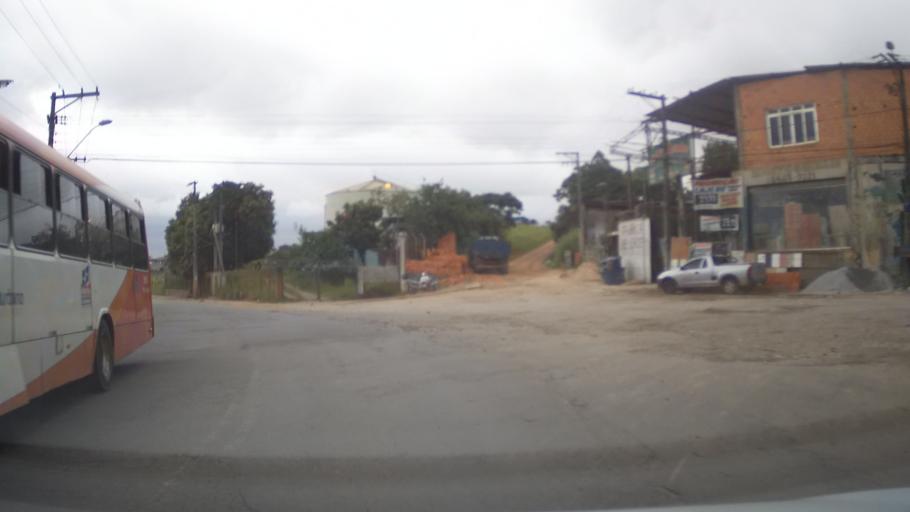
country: BR
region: Sao Paulo
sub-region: Guarulhos
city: Guarulhos
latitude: -23.4077
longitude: -46.4415
